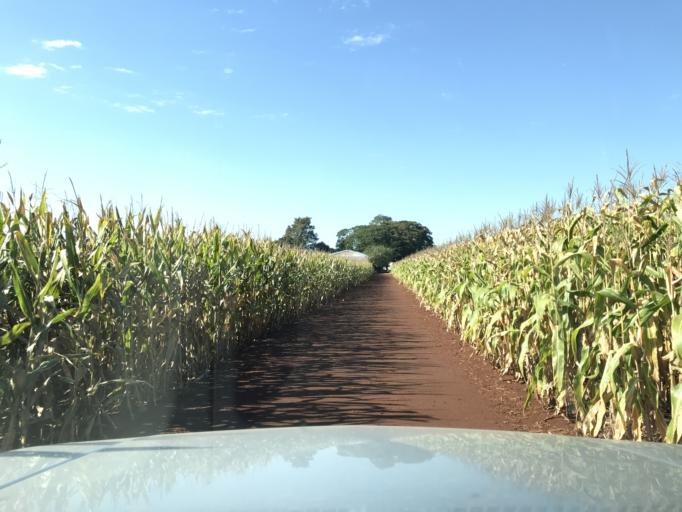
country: BR
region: Parana
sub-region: Palotina
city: Palotina
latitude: -24.2639
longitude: -53.8060
